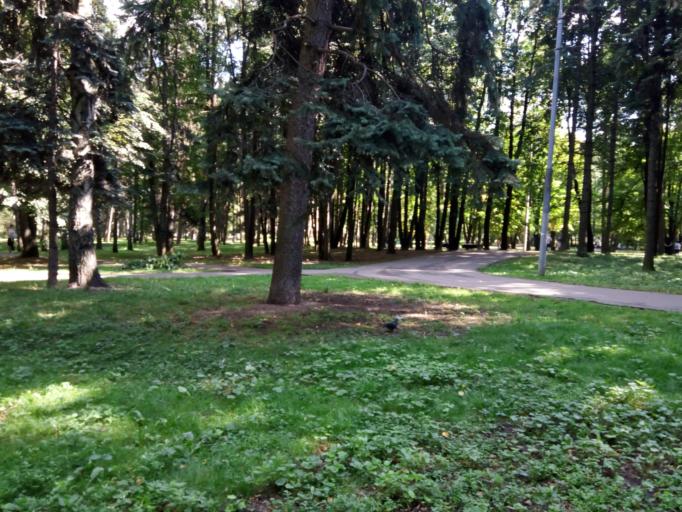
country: RU
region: Moskovskaya
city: Levoberezhnyy
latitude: 55.8534
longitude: 37.4743
